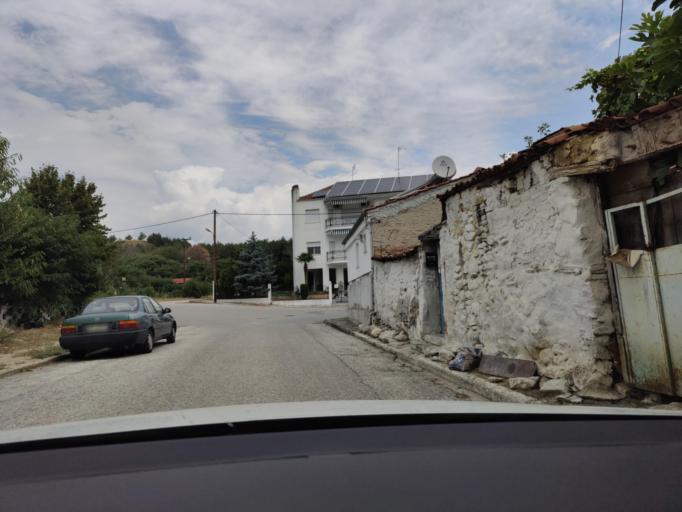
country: GR
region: Central Macedonia
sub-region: Nomos Serron
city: Serres
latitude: 41.0877
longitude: 23.5325
